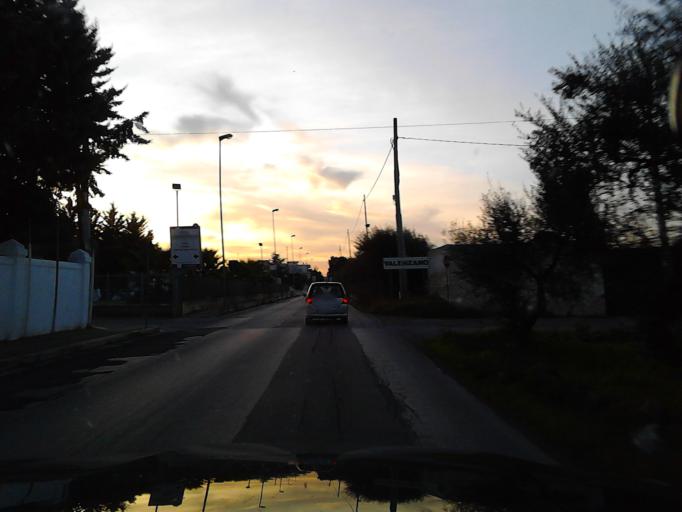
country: IT
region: Apulia
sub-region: Provincia di Bari
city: Valenzano
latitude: 41.0452
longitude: 16.8956
